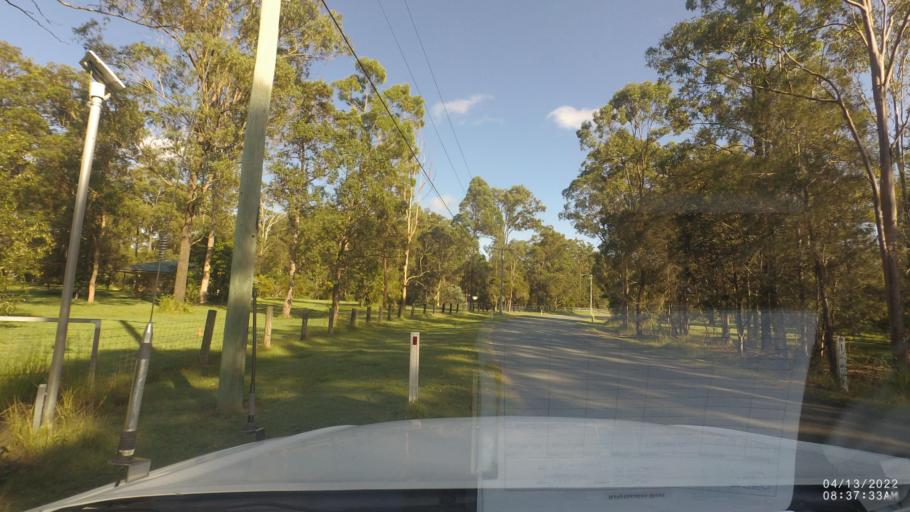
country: AU
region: Queensland
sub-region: Logan
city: Chambers Flat
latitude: -27.7939
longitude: 153.1185
